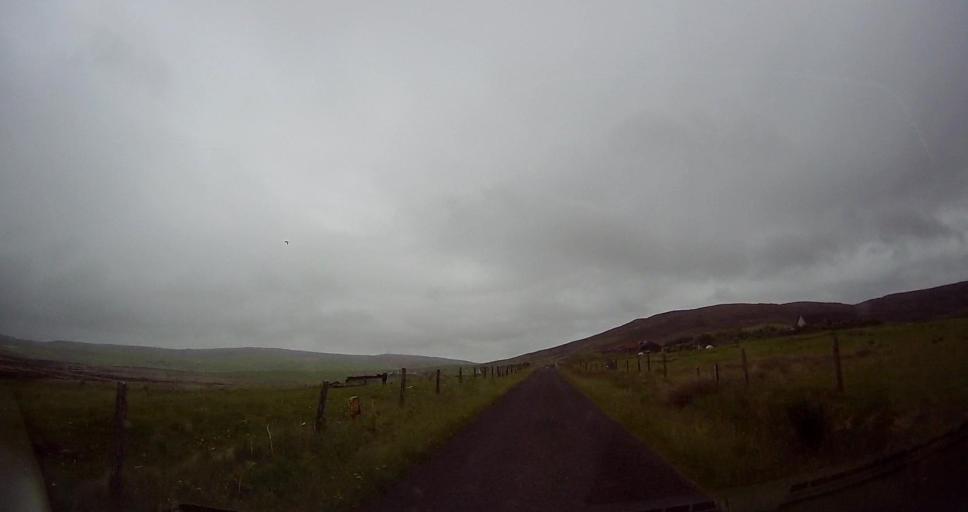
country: GB
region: Scotland
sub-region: Orkney Islands
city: Stromness
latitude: 58.9780
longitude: -3.1704
